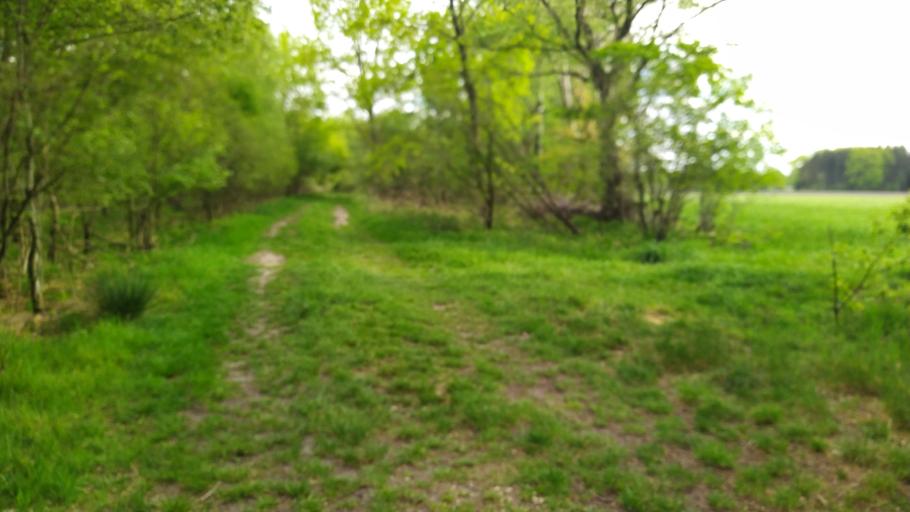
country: DE
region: Lower Saxony
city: Brest
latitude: 53.4301
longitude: 9.3906
